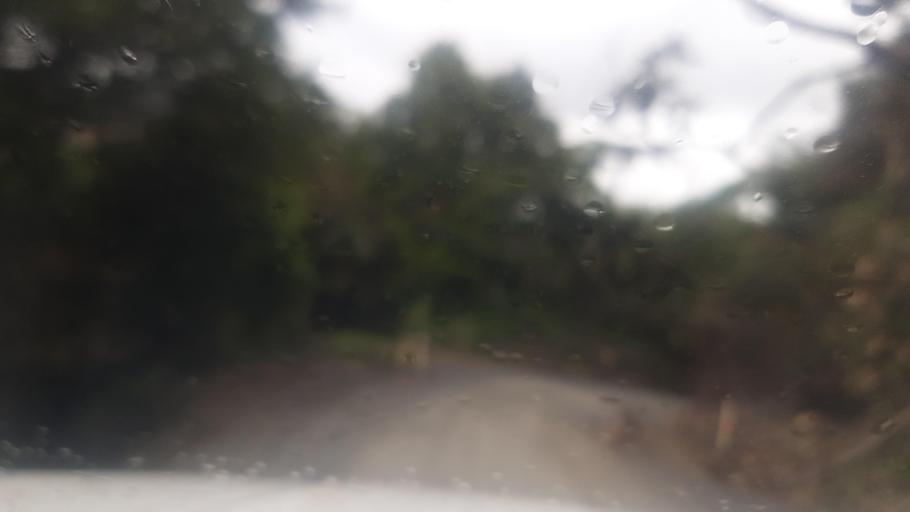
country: NZ
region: Northland
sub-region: Far North District
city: Taipa
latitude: -35.0910
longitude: 173.3935
